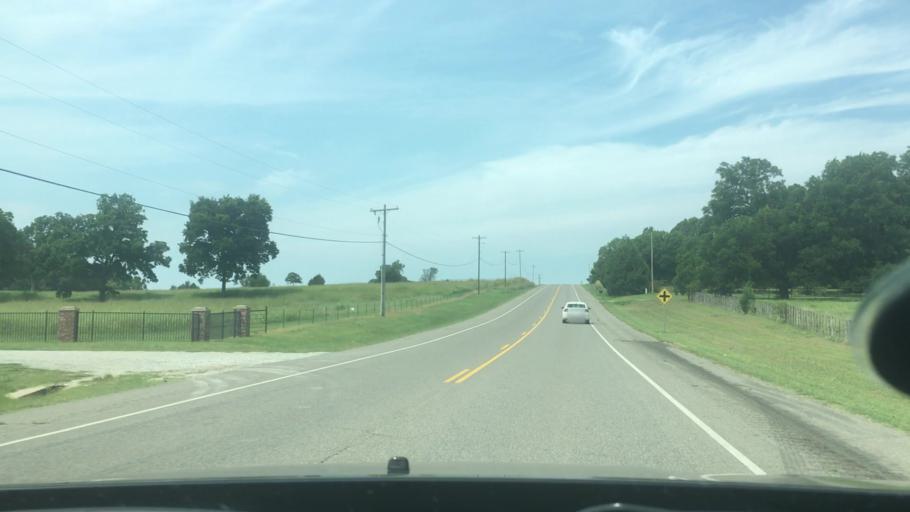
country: US
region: Oklahoma
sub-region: Pottawatomie County
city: Shawnee
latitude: 35.3331
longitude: -96.8170
